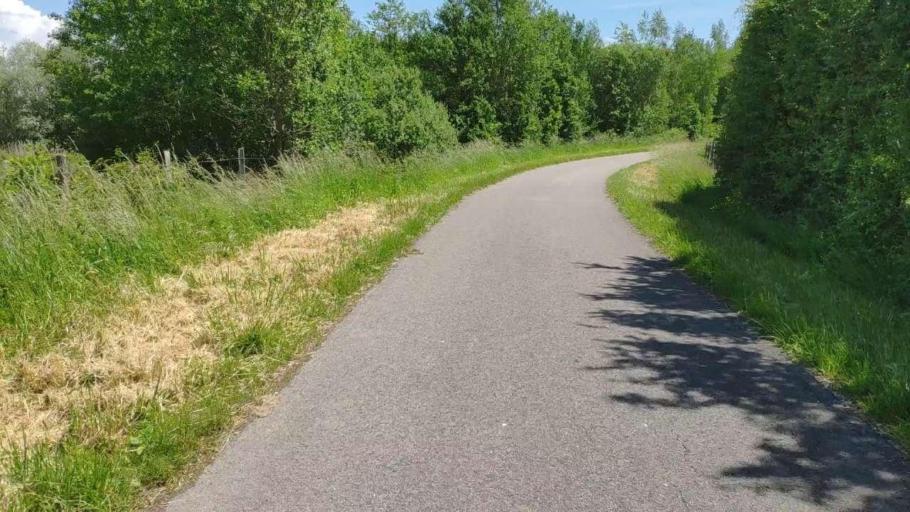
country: FR
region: Franche-Comte
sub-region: Departement du Jura
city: Bletterans
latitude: 46.7848
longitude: 5.4515
